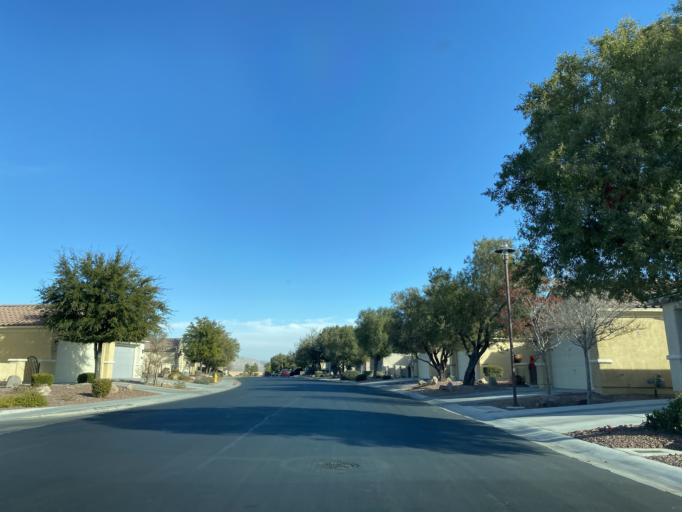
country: US
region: Nevada
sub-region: Clark County
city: North Las Vegas
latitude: 36.3205
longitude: -115.2488
